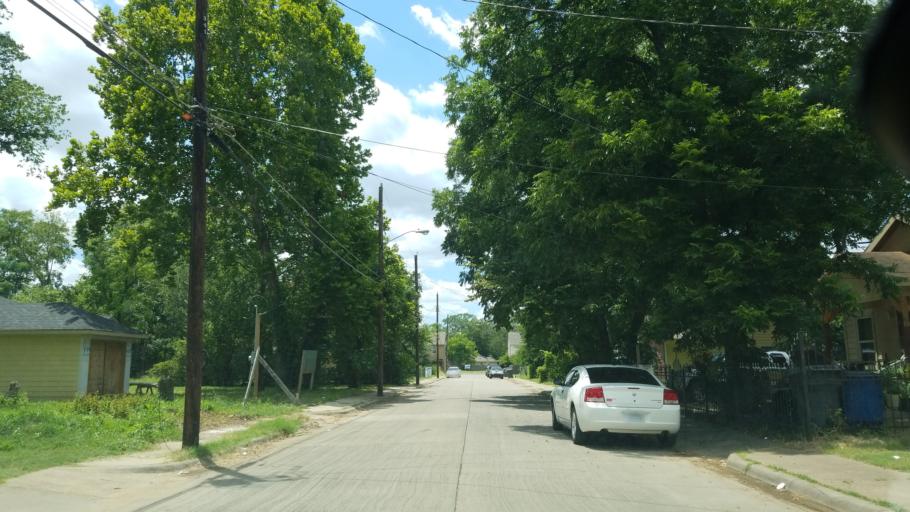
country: US
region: Texas
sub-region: Dallas County
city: Dallas
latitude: 32.7487
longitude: -96.7515
